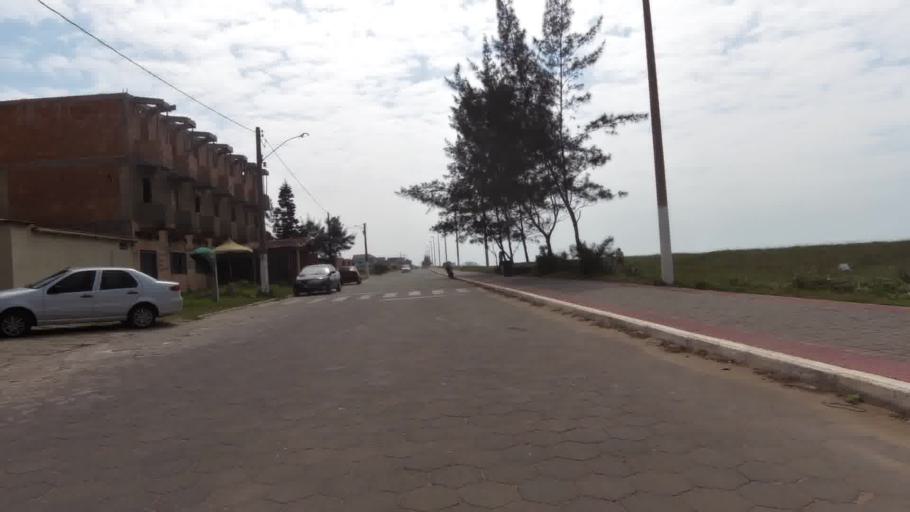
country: BR
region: Espirito Santo
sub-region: Marataizes
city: Marataizes
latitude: -21.0221
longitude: -40.8111
